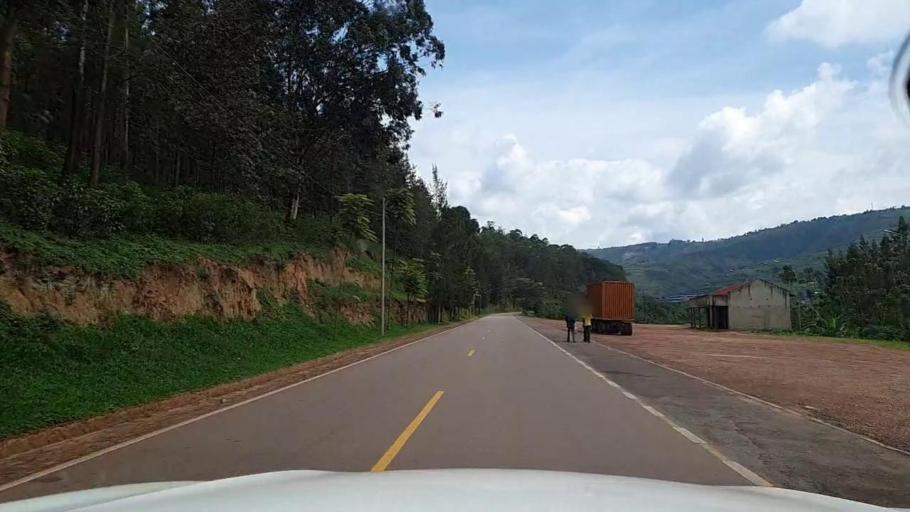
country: RW
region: Kigali
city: Kigali
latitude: -1.8617
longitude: 30.0890
